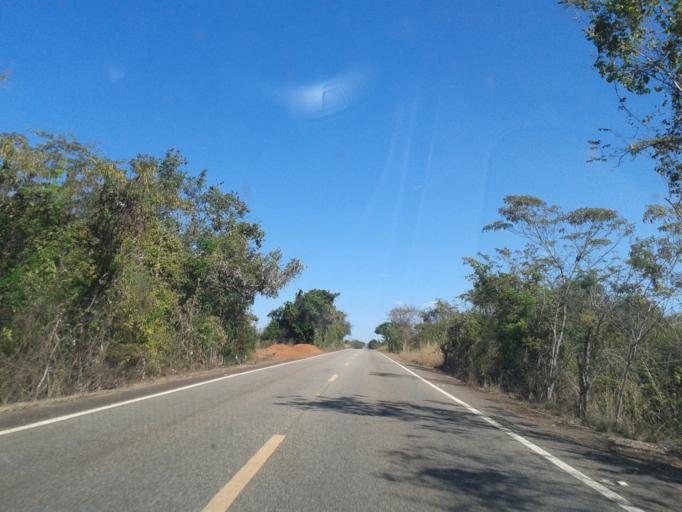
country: BR
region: Goias
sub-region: Sao Miguel Do Araguaia
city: Sao Miguel do Araguaia
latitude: -13.6807
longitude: -50.3303
